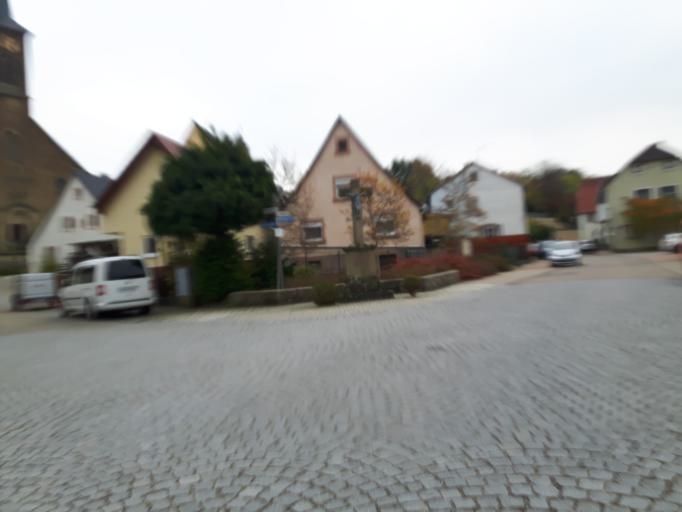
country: DE
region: Baden-Wuerttemberg
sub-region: Karlsruhe Region
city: Zaisenhausen
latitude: 49.1750
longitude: 8.7965
